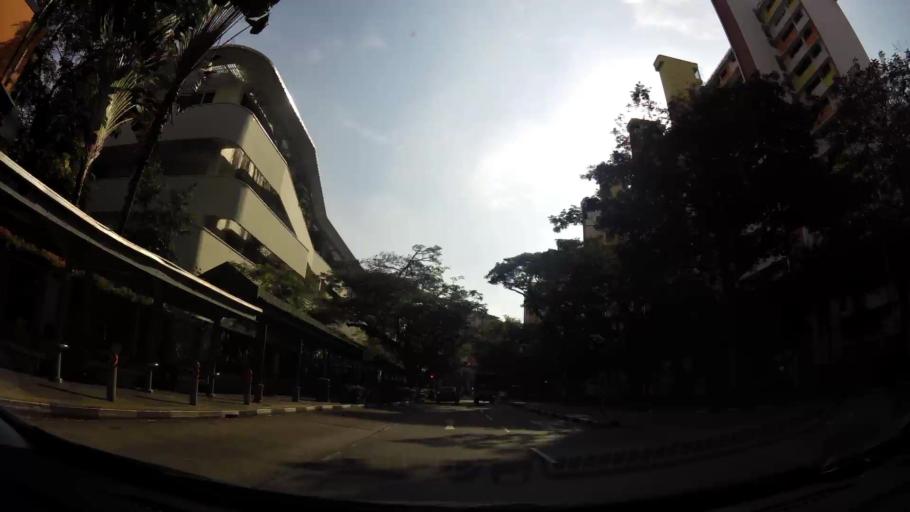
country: SG
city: Singapore
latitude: 1.3398
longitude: 103.8565
